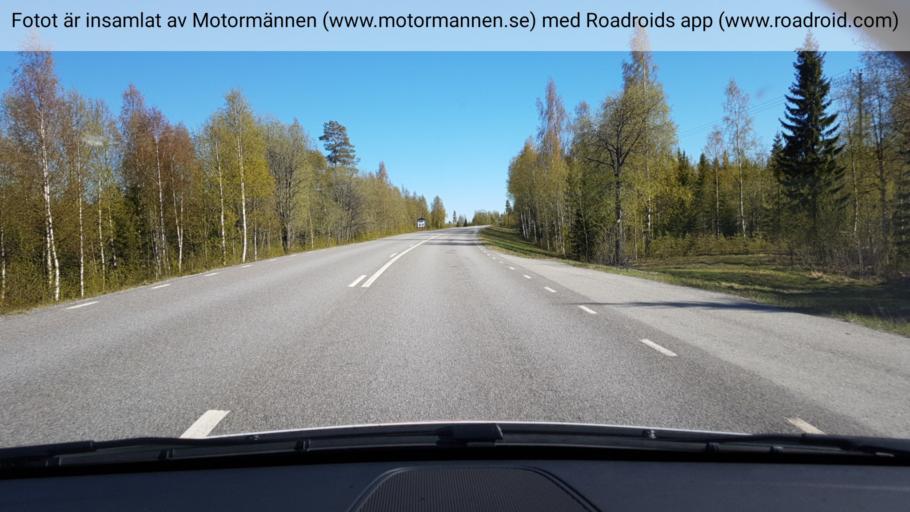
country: SE
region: Jaemtland
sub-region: Stroemsunds Kommun
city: Stroemsund
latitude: 64.3147
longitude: 15.2130
